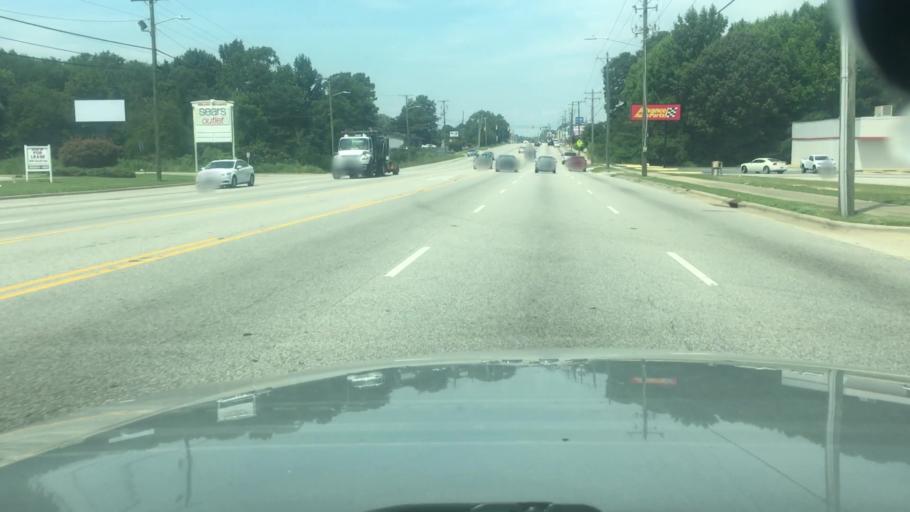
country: US
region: North Carolina
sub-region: Cumberland County
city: Fayetteville
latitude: 35.0437
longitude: -78.9484
